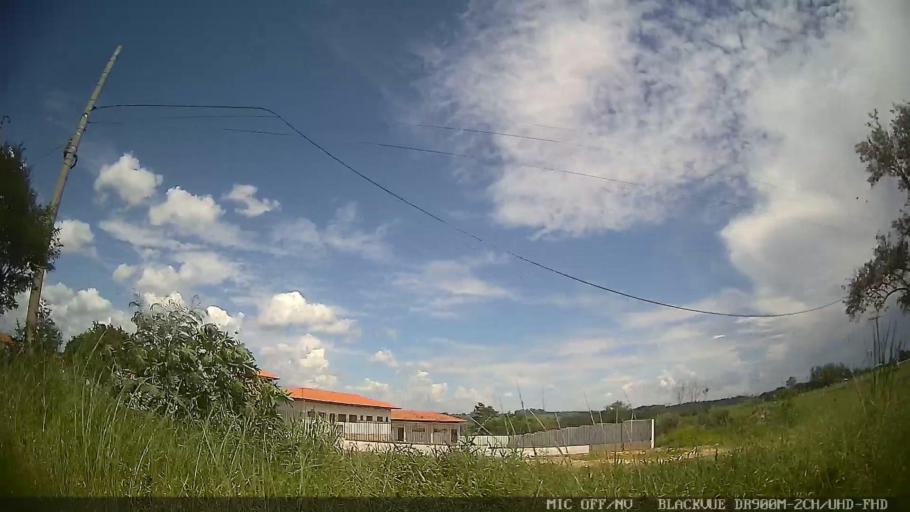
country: BR
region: Sao Paulo
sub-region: Conchas
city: Conchas
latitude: -23.0407
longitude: -48.0210
